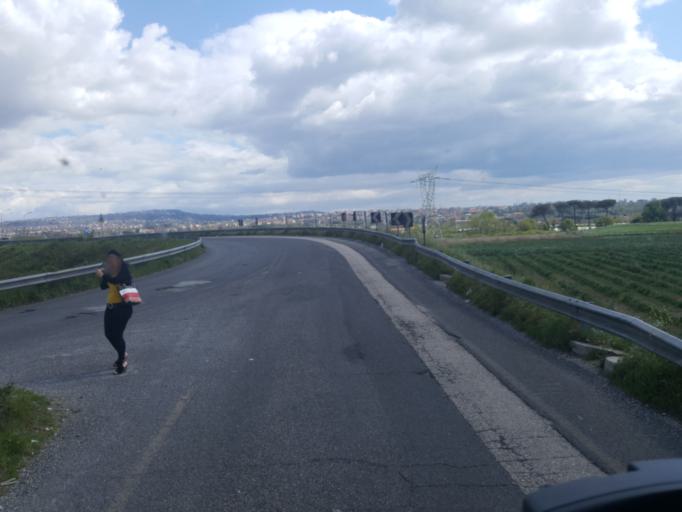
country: IT
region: Campania
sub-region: Provincia di Napoli
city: Torretta-Scalzapecora
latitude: 40.9298
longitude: 14.1208
